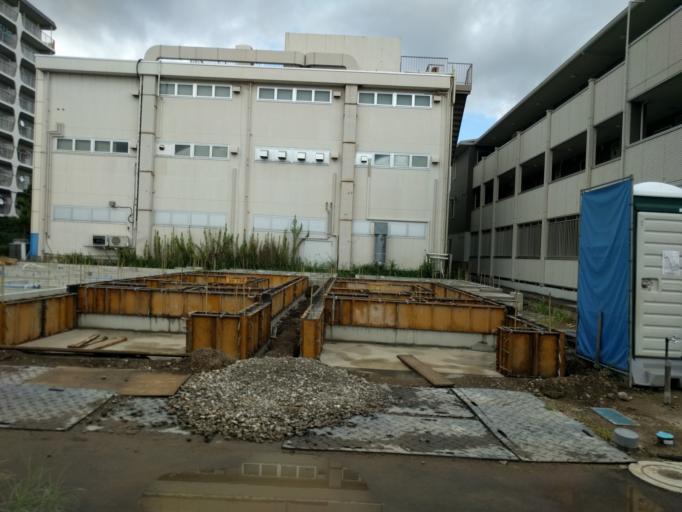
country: JP
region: Saitama
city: Shimotoda
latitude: 35.8339
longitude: 139.6699
